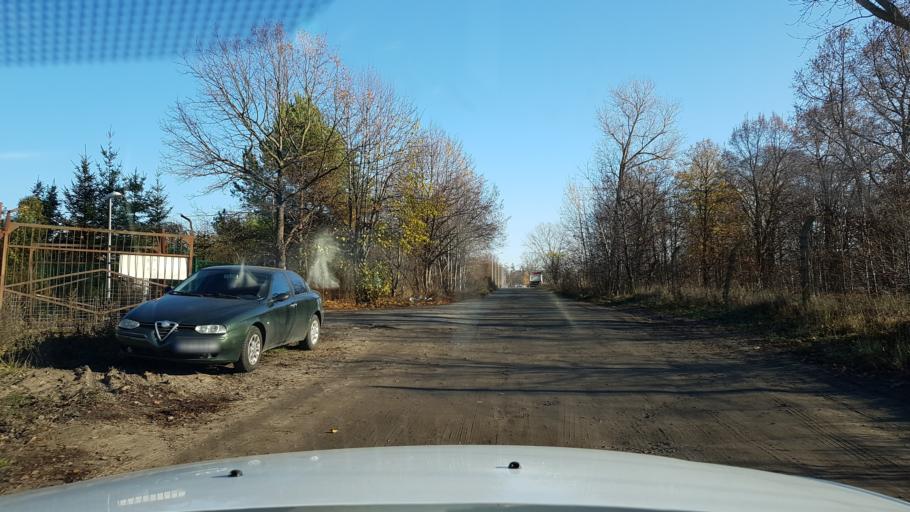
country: PL
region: West Pomeranian Voivodeship
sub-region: Powiat stargardzki
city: Stargard Szczecinski
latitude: 53.3354
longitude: 14.9984
